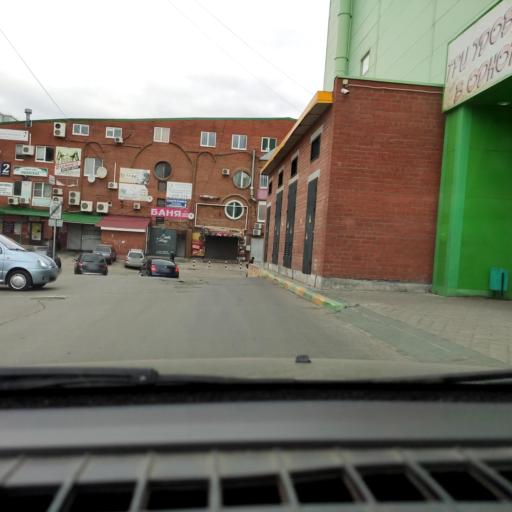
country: RU
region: Samara
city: Tol'yatti
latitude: 53.5438
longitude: 49.3594
